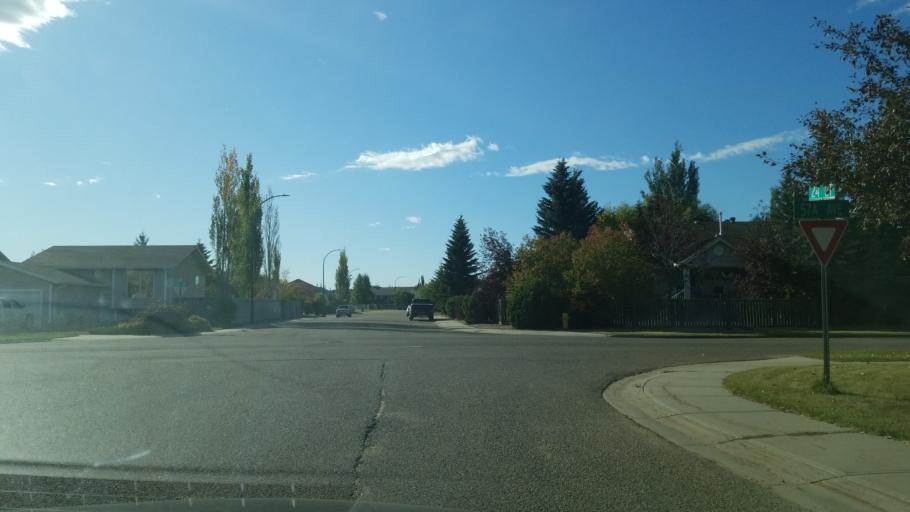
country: CA
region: Saskatchewan
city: Lloydminster
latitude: 53.2586
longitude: -110.0234
